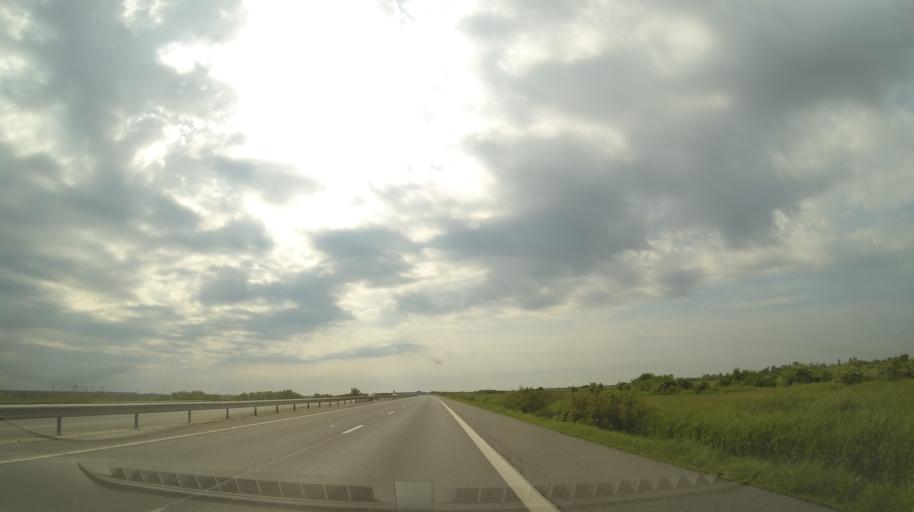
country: RO
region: Dambovita
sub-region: Comuna Mogosani
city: Zavoiu
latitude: 44.6360
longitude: 25.4062
